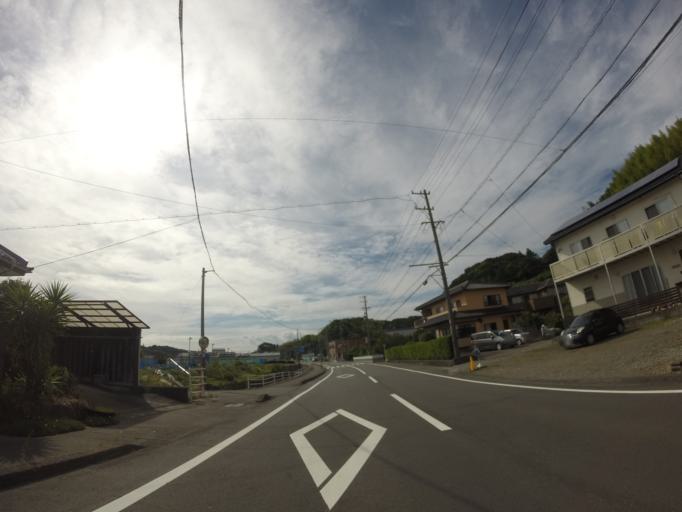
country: JP
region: Shizuoka
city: Shimada
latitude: 34.7655
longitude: 138.1925
